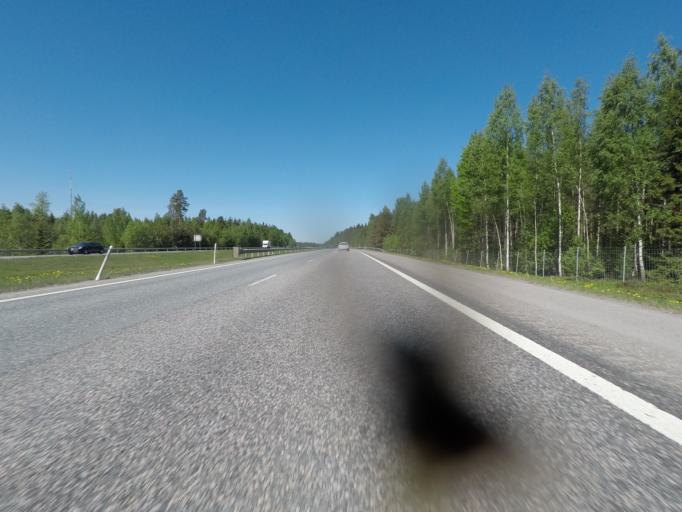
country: FI
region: Haeme
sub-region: Haemeenlinna
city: Haemeenlinna
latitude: 60.9499
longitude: 24.5016
